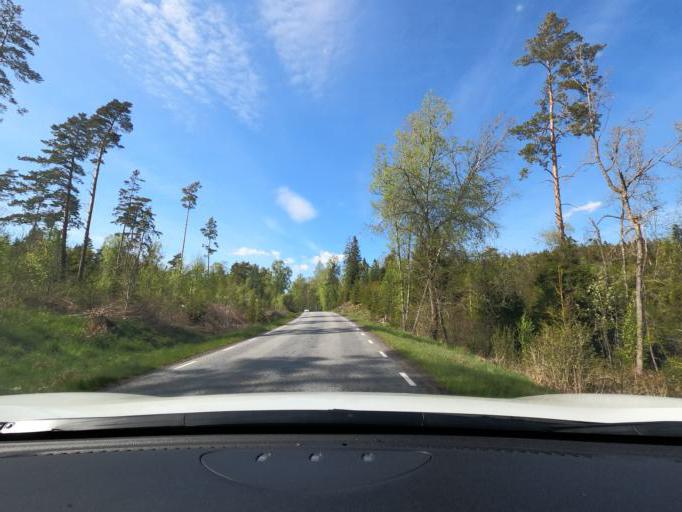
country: SE
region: Vaestra Goetaland
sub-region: Marks Kommun
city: Bua
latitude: 57.4872
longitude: 12.5646
